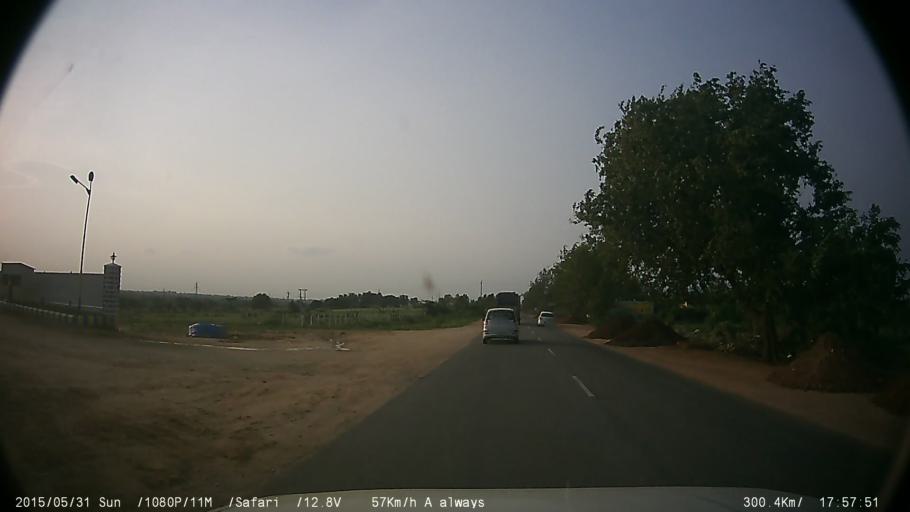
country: IN
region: Karnataka
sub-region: Mysore
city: Nanjangud
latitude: 12.0046
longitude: 76.6692
